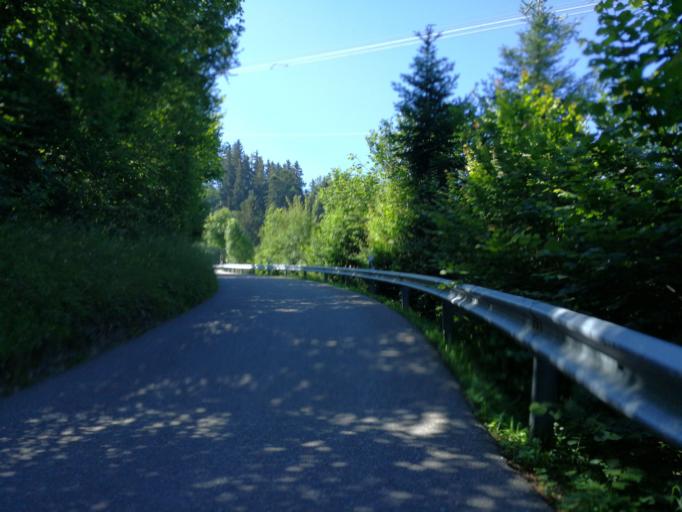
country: CH
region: Zurich
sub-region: Bezirk Hinwil
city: Hadlikon
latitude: 47.2904
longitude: 8.8811
